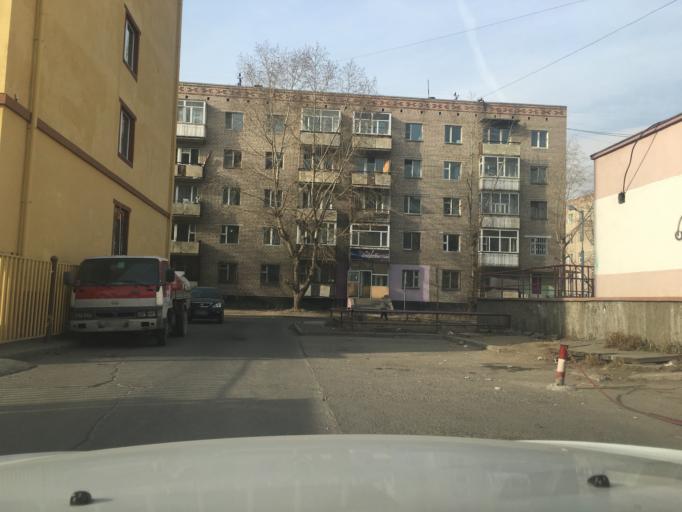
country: MN
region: Ulaanbaatar
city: Ulaanbaatar
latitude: 47.9119
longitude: 106.8827
